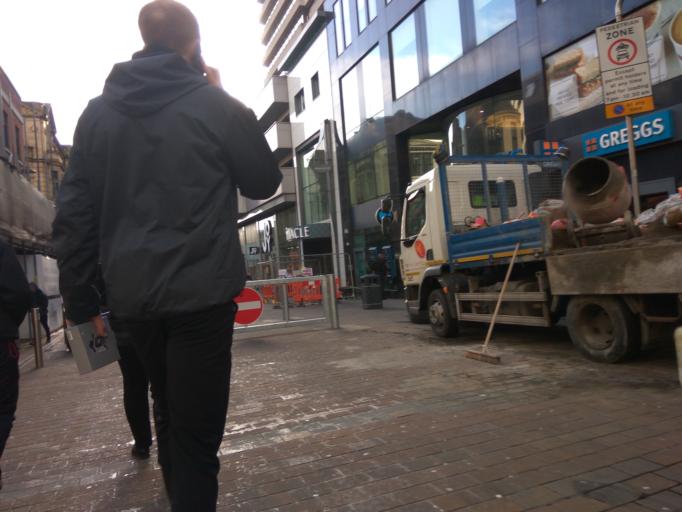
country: GB
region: England
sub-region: City and Borough of Leeds
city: Leeds
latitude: 53.7982
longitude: -1.5451
